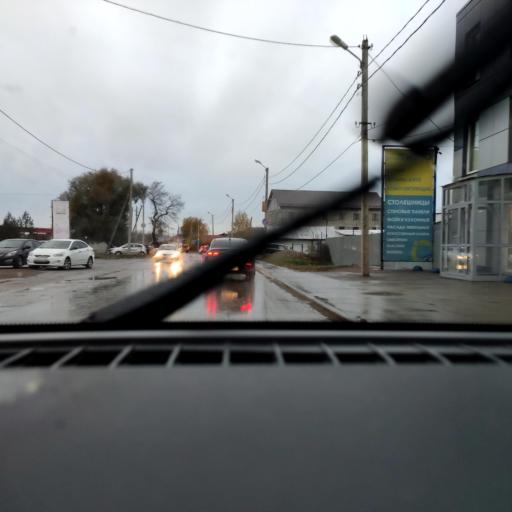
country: RU
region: Perm
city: Kondratovo
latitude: 57.9529
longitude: 56.1366
